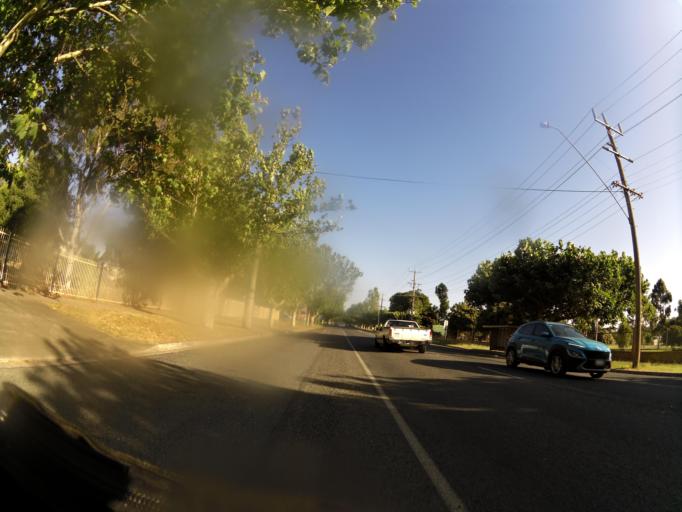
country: AU
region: Victoria
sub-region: Murrindindi
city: Kinglake West
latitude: -37.0213
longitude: 145.1307
